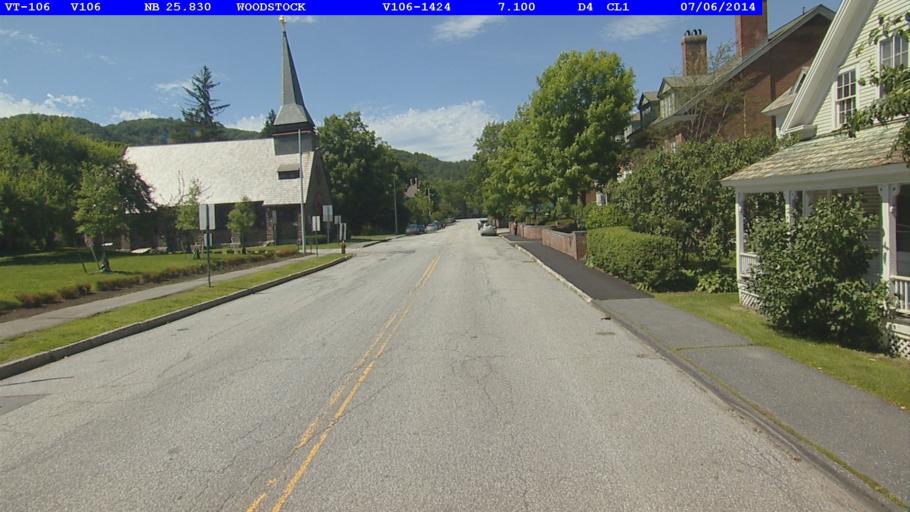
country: US
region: Vermont
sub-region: Windsor County
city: Woodstock
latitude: 43.6221
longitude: -72.5190
